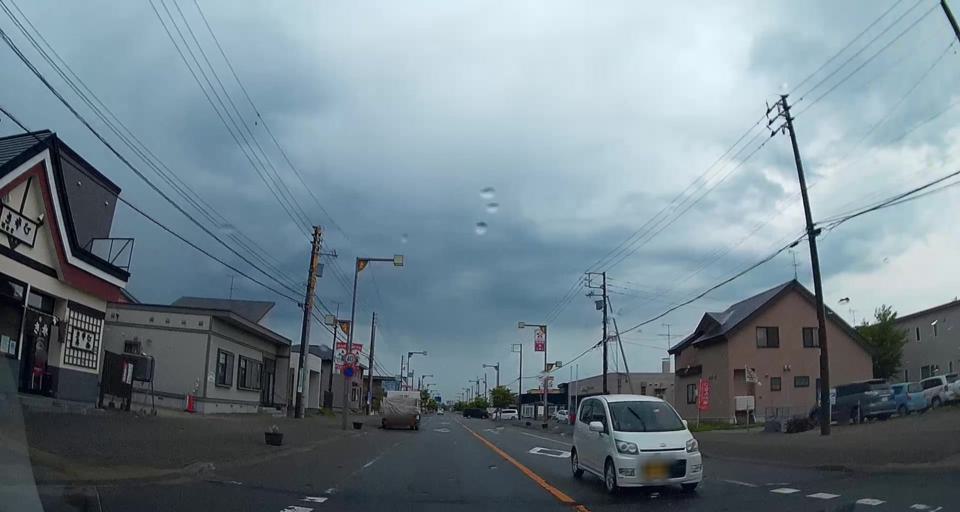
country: JP
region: Hokkaido
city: Chitose
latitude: 42.7249
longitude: 141.8778
